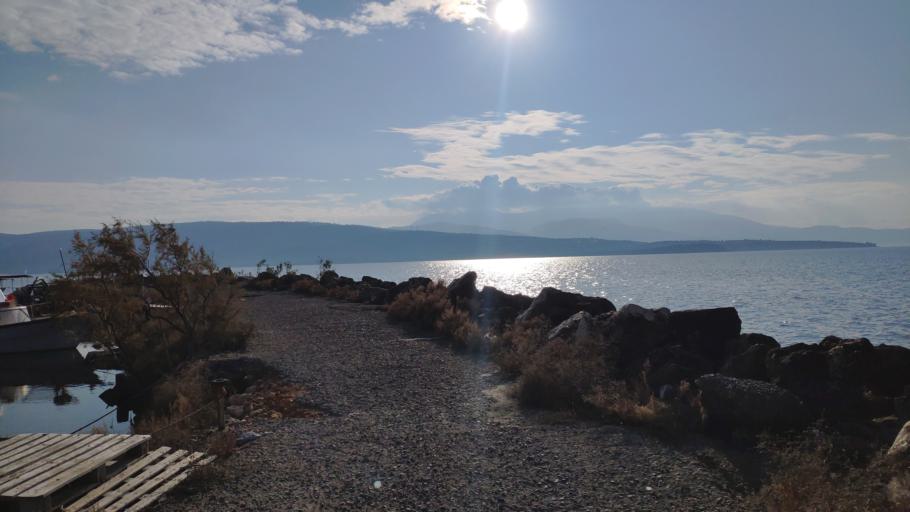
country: GR
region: West Greece
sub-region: Nomos Aitolias kai Akarnanias
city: Krikellos
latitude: 38.9275
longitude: 21.1396
